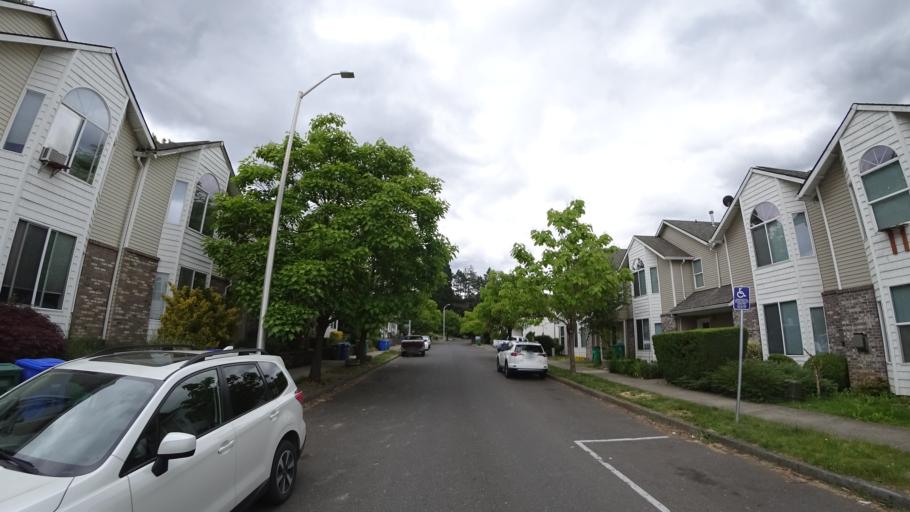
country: US
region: Oregon
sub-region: Clackamas County
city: Happy Valley
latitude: 45.4848
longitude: -122.5230
